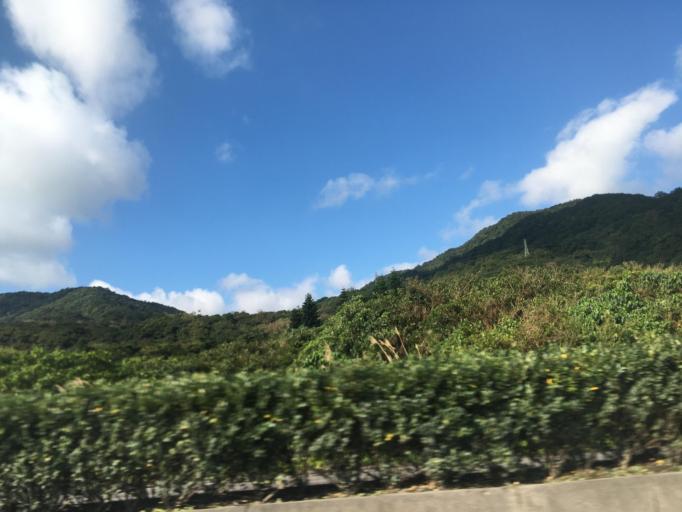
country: TW
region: Taiwan
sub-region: Yilan
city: Yilan
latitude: 24.9296
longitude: 121.8853
